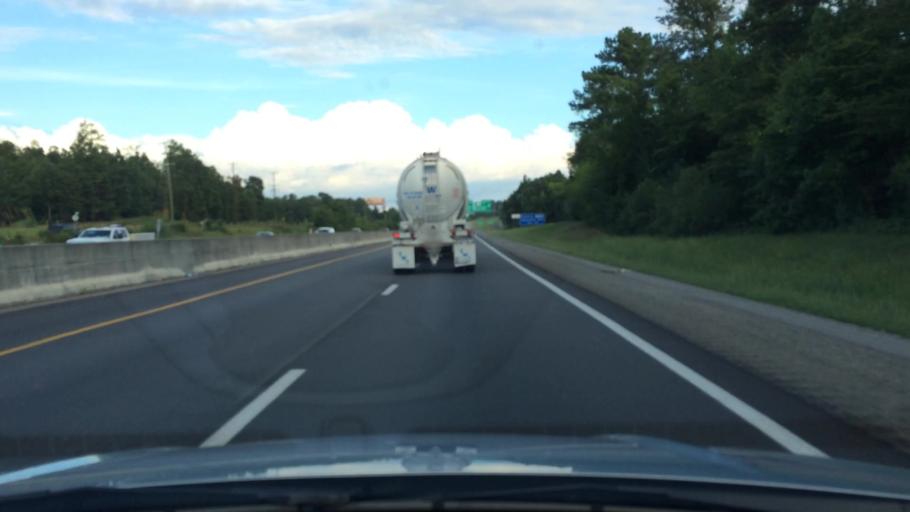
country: US
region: South Carolina
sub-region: Lexington County
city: Irmo
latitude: 34.1053
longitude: -81.1816
